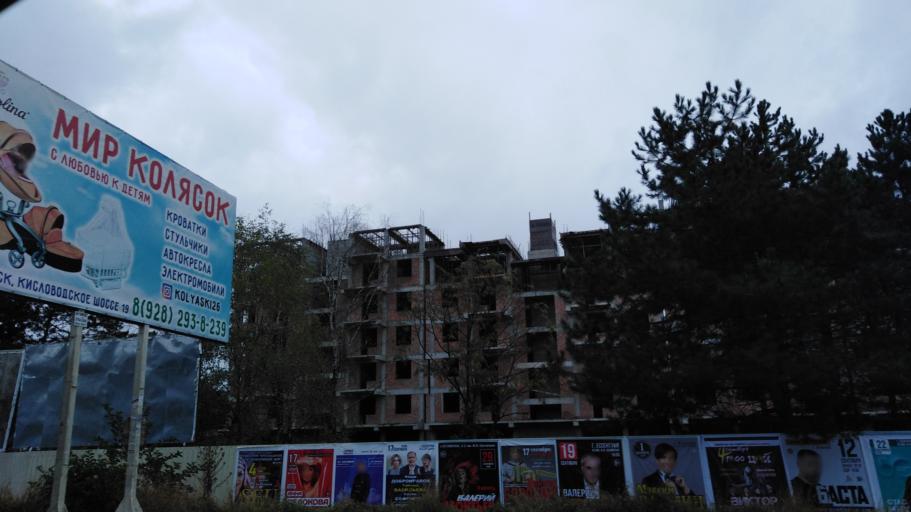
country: RU
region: Stavropol'skiy
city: Yessentukskaya
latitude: 44.0511
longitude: 42.8988
